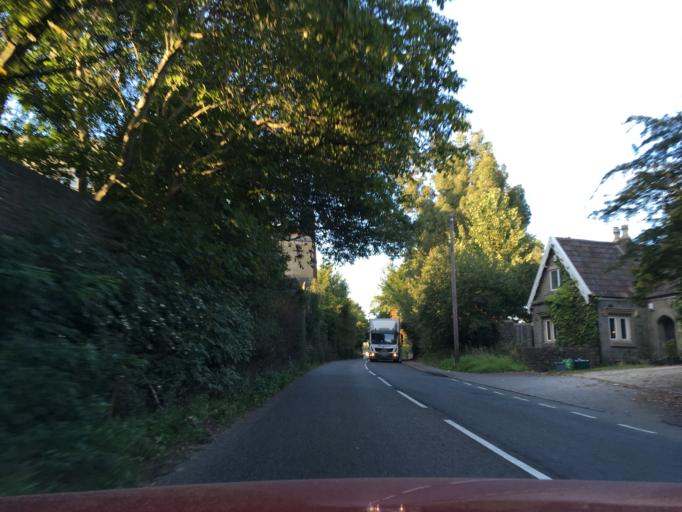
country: GB
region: England
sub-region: South Gloucestershire
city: Winterbourne
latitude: 51.5065
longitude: -2.5195
